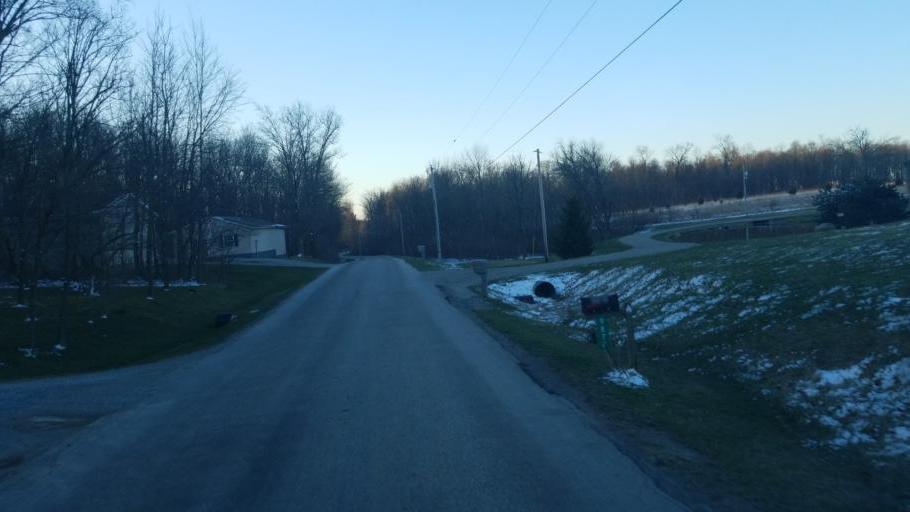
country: US
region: Ohio
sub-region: Highland County
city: Leesburg
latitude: 39.2827
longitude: -83.5032
